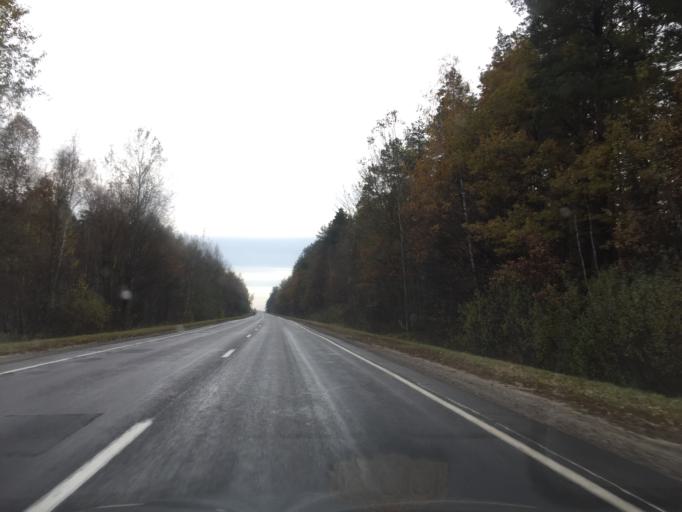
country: BY
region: Gomel
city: Kastsyukowka
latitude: 52.4250
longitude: 30.8283
